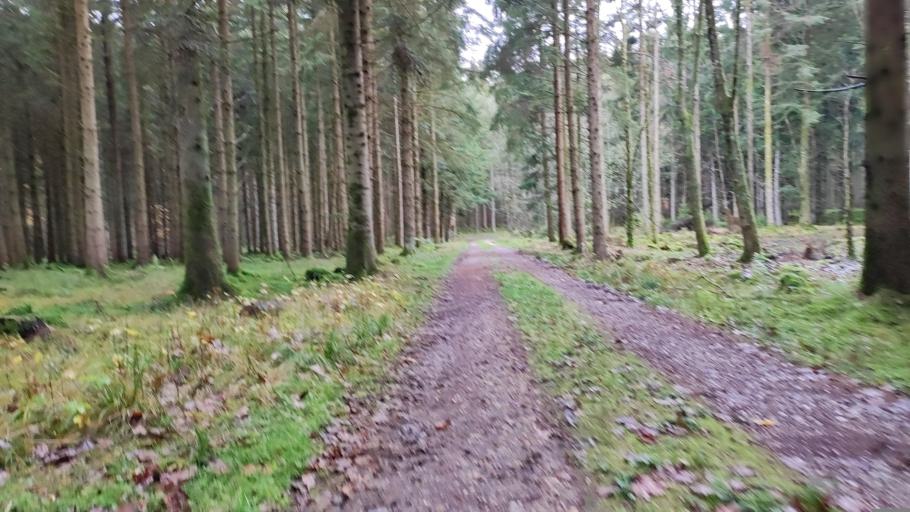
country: DE
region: Bavaria
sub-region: Swabia
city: Ziemetshausen
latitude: 48.3362
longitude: 10.5176
